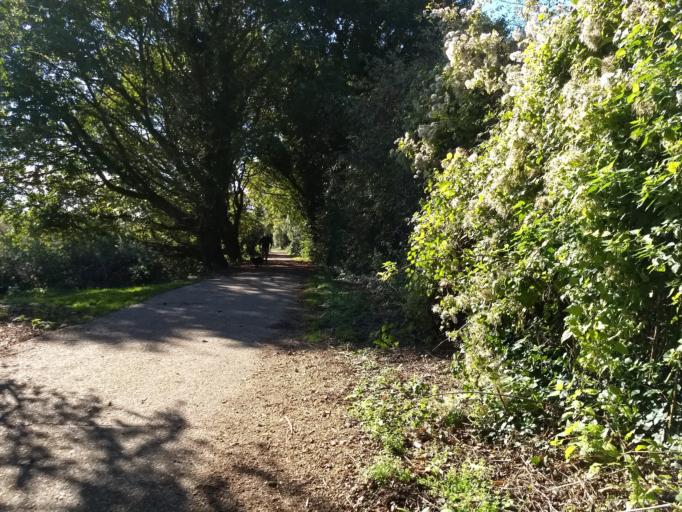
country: GB
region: England
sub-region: Isle of Wight
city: Ventnor
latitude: 50.6247
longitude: -1.2228
